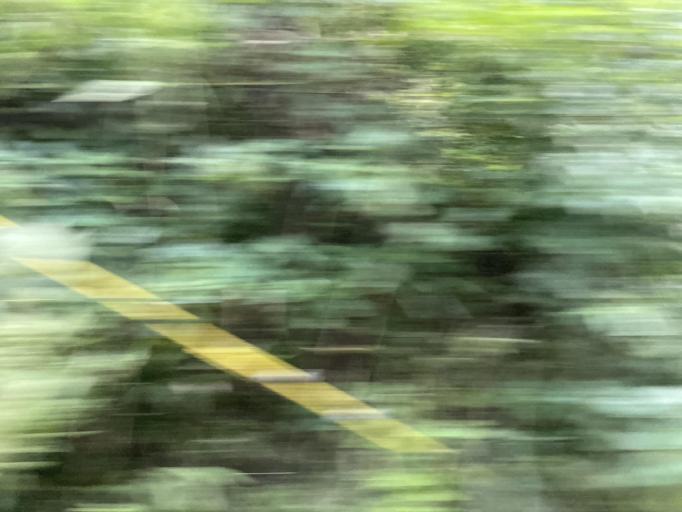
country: JP
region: Nara
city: Sakurai
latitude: 34.5218
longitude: 135.8868
